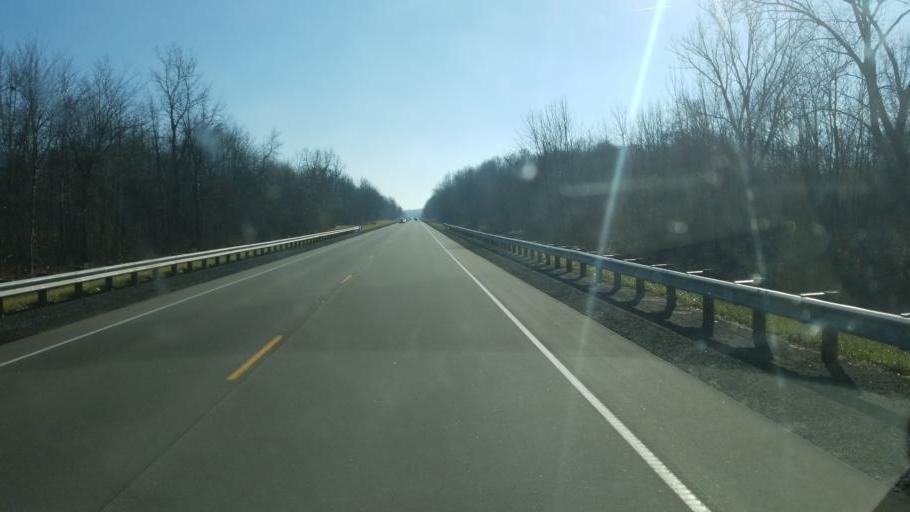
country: US
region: Ohio
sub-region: Lake County
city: Painesville
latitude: 41.6341
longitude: -81.2403
